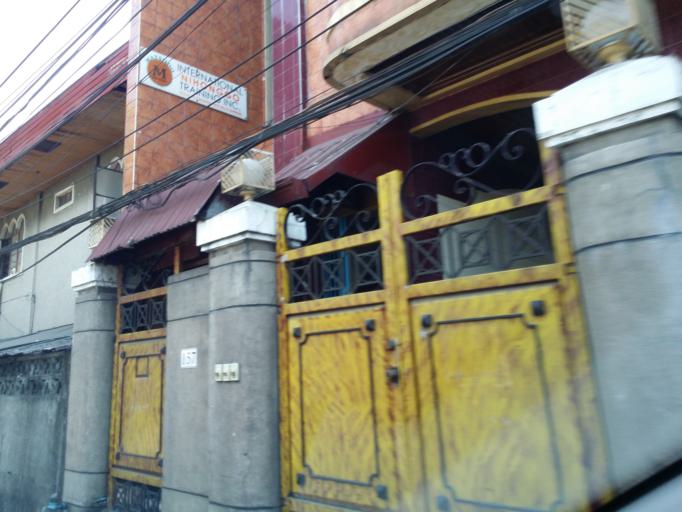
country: PH
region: Metro Manila
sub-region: Mandaluyong
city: Mandaluyong City
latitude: 14.5797
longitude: 121.0262
